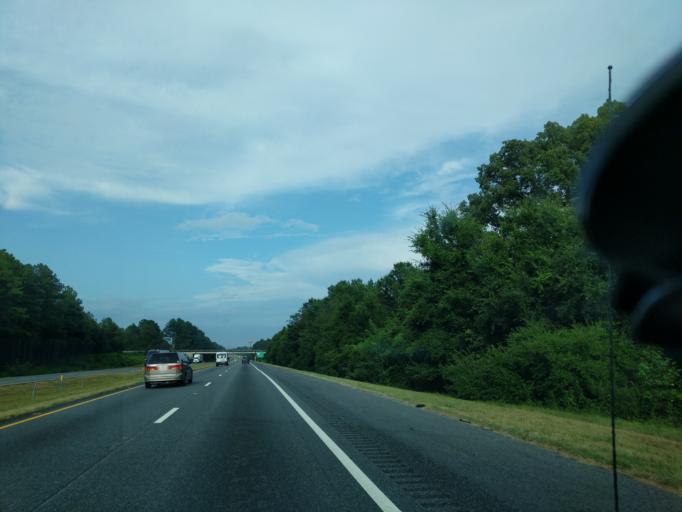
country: US
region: Georgia
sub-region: Hart County
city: Reed Creek
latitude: 34.5023
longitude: -82.9825
